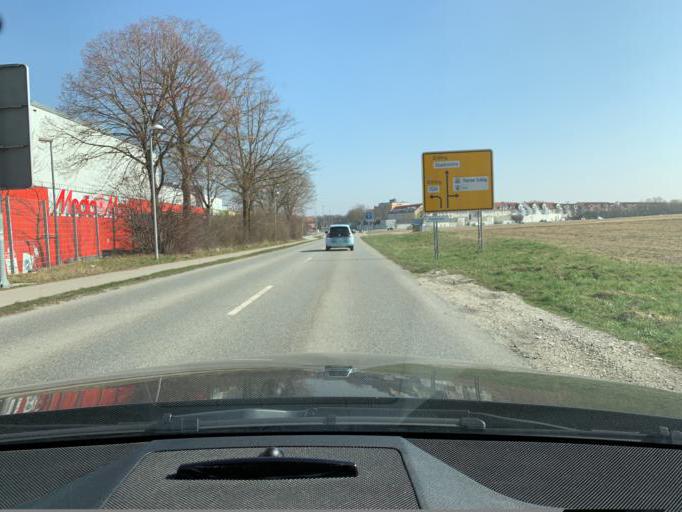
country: DE
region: Bavaria
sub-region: Upper Bavaria
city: Erding
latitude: 48.3056
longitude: 11.8891
